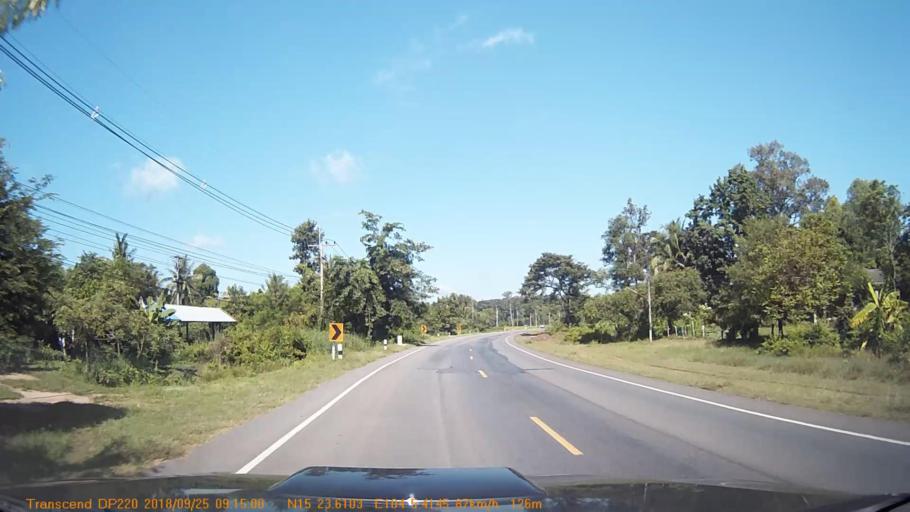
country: TH
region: Sisaket
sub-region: Amphoe Bueng Bun
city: Bueng Bun
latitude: 15.3935
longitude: 104.0902
